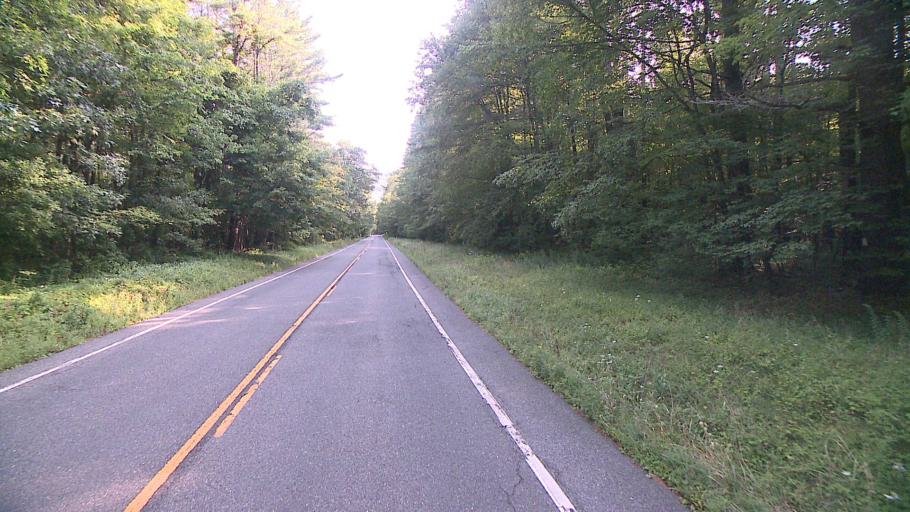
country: US
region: Connecticut
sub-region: Litchfield County
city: Kent
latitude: 41.8438
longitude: -73.3781
